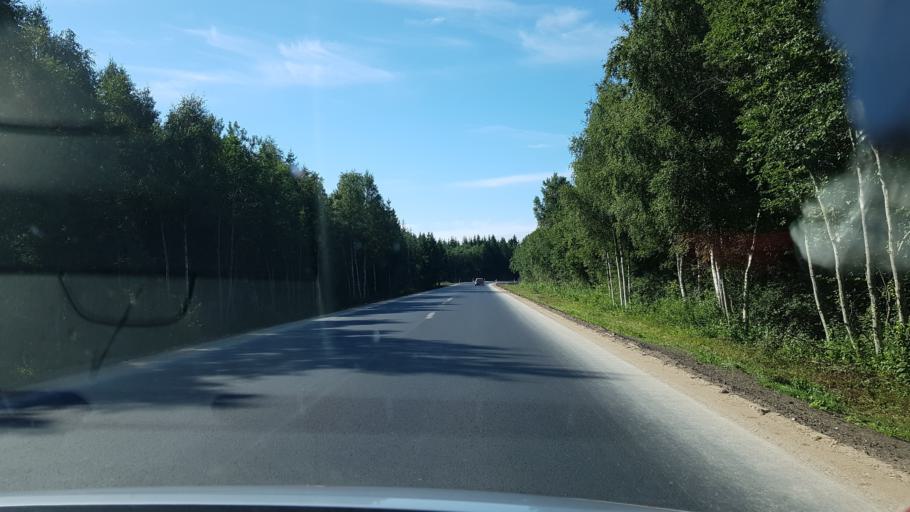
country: EE
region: Laeaene
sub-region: Ridala Parish
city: Uuemoisa
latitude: 59.0093
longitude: 23.7823
